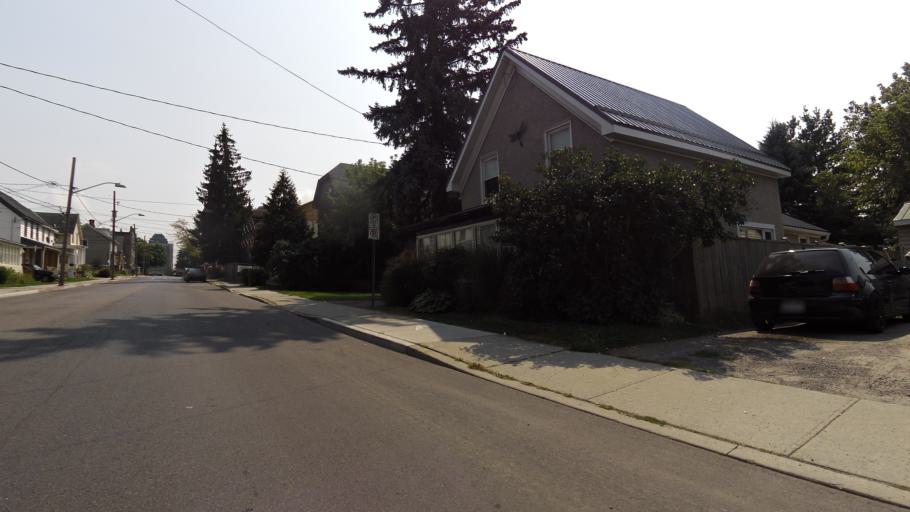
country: CA
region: Ontario
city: Brockville
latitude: 44.5918
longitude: -75.6877
